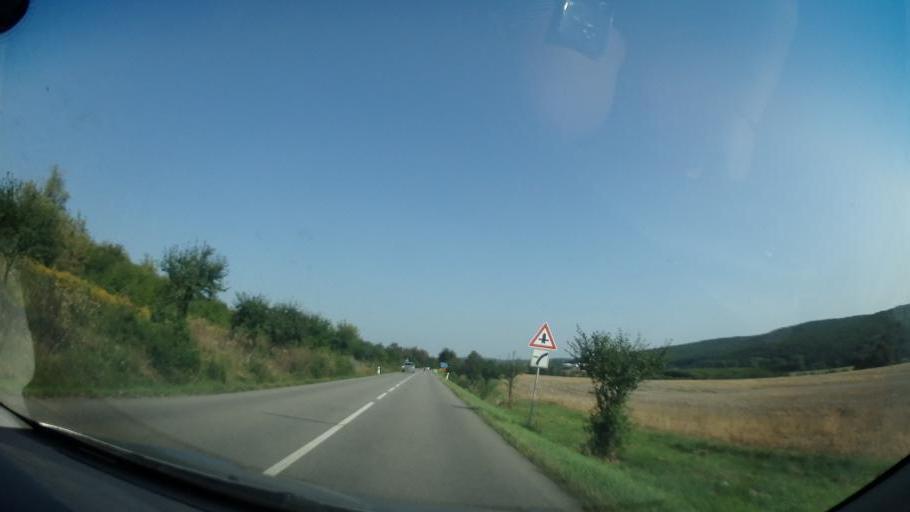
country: CZ
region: South Moravian
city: Kurim
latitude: 49.2525
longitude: 16.5245
